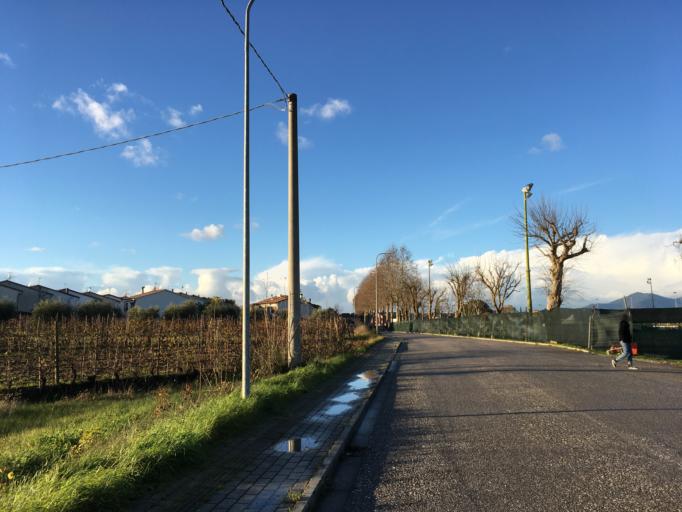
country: IT
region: Tuscany
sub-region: Province of Pisa
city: Cenaia
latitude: 43.6036
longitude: 10.5431
